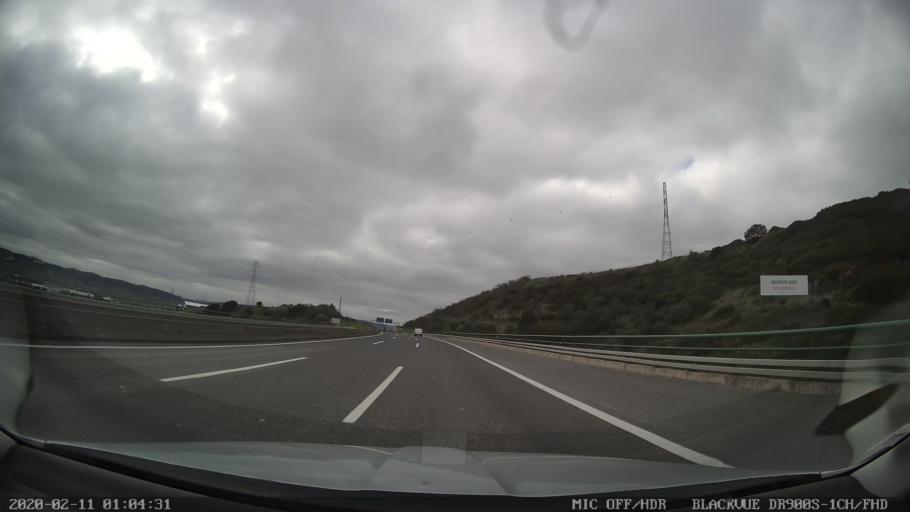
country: PT
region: Lisbon
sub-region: Loures
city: Santo Antao do Tojal
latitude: 38.8746
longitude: -9.1349
